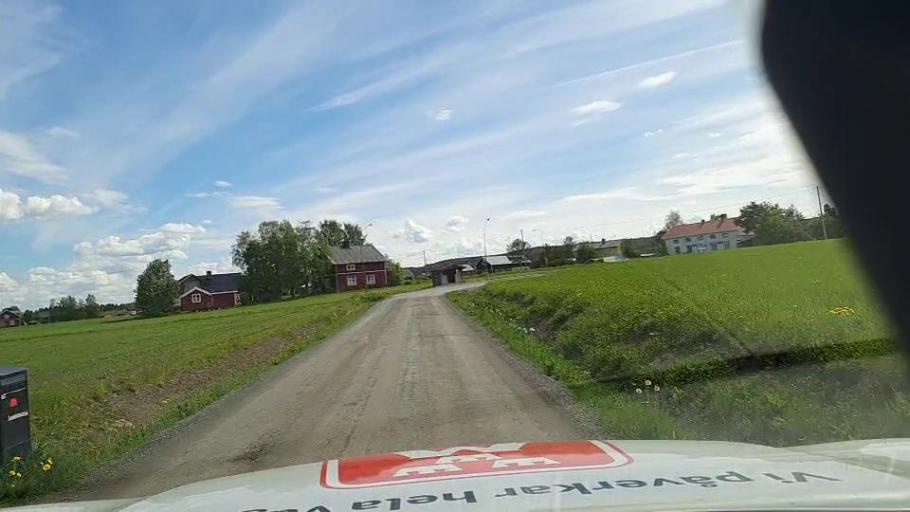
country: SE
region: Jaemtland
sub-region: OEstersunds Kommun
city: Brunflo
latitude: 62.9884
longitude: 14.8095
